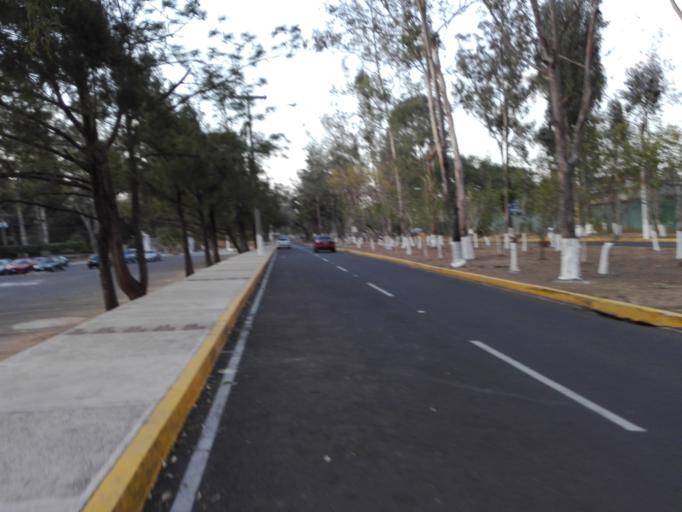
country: GT
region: Guatemala
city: Santa Catarina Pinula
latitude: 14.5842
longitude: -90.5520
